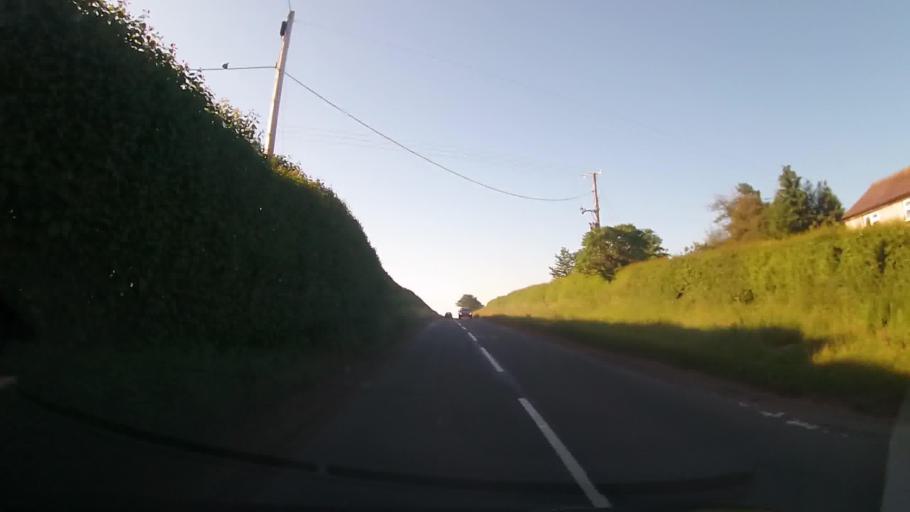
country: GB
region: England
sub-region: Shropshire
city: Shawbury
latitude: 52.8184
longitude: -2.6670
